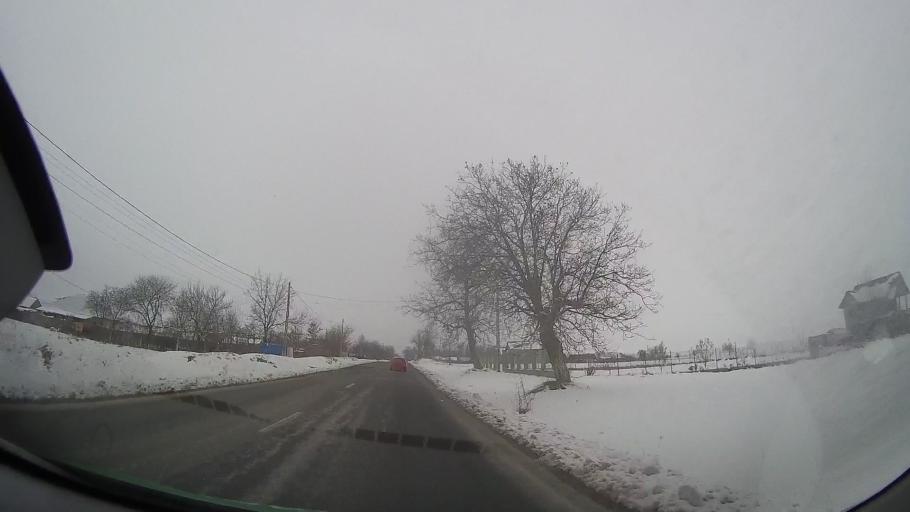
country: RO
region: Vaslui
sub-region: Comuna Negresti
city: Negresti
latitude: 46.8393
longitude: 27.4226
